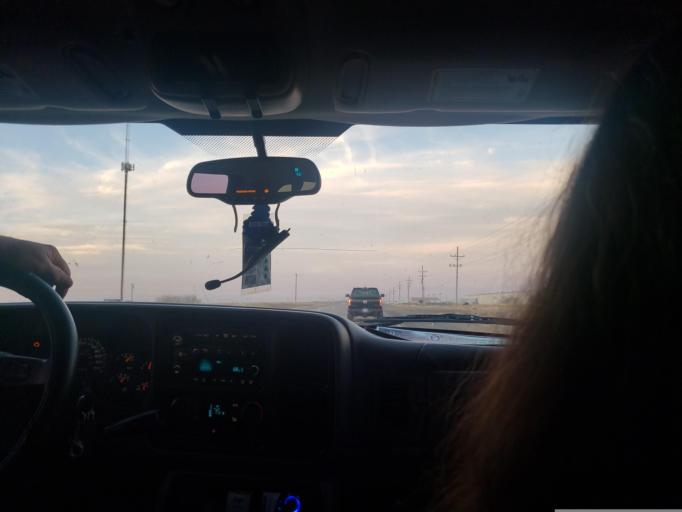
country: US
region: Kansas
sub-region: Seward County
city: Liberal
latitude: 37.0593
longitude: -100.9043
